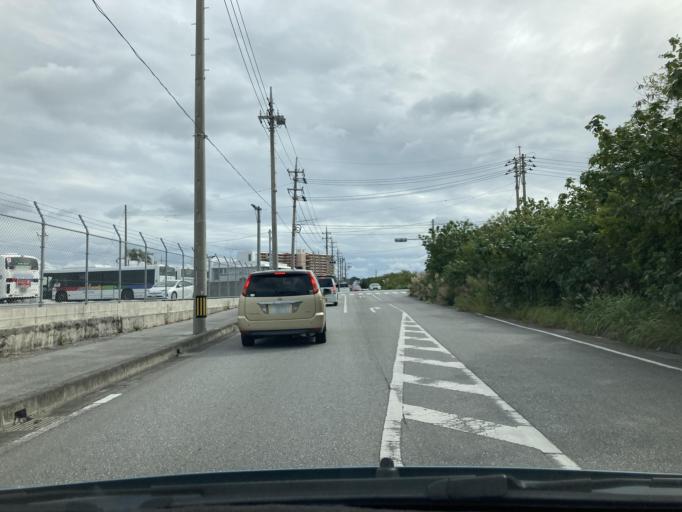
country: JP
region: Okinawa
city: Itoman
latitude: 26.1549
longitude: 127.6677
